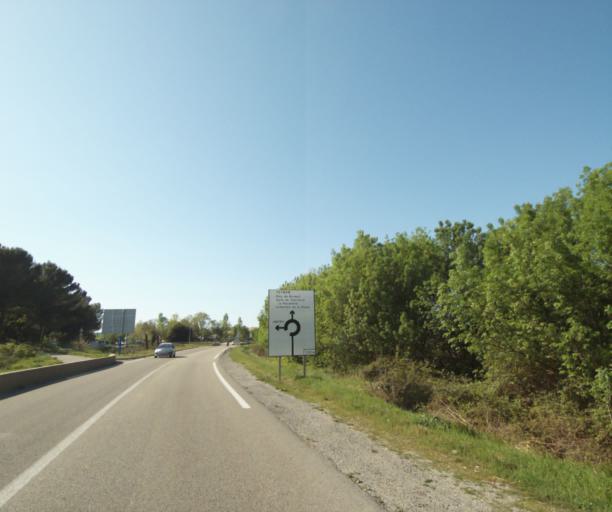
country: FR
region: Languedoc-Roussillon
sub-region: Departement de l'Herault
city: Jacou
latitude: 43.6613
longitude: 3.9272
